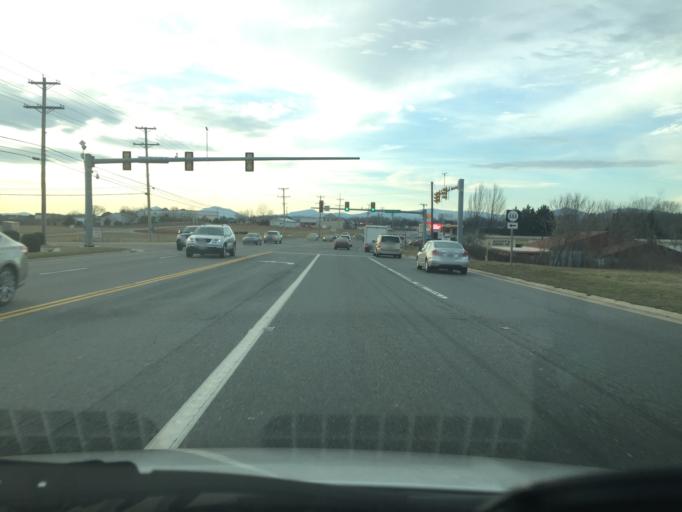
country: US
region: Virginia
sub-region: Bedford County
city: Forest
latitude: 37.3670
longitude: -79.2969
